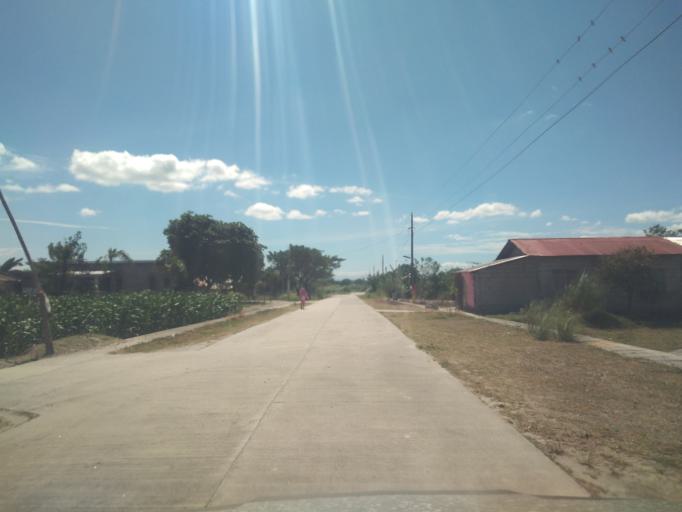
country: PH
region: Central Luzon
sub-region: Province of Pampanga
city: San Basilio
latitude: 15.0301
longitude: 120.6057
